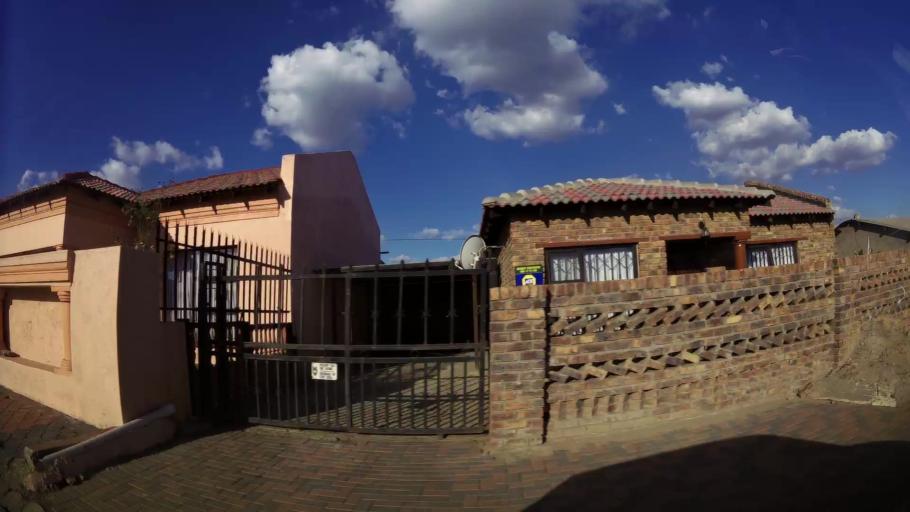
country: ZA
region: Mpumalanga
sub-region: Nkangala District Municipality
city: Witbank
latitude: -25.8725
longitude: 29.1849
